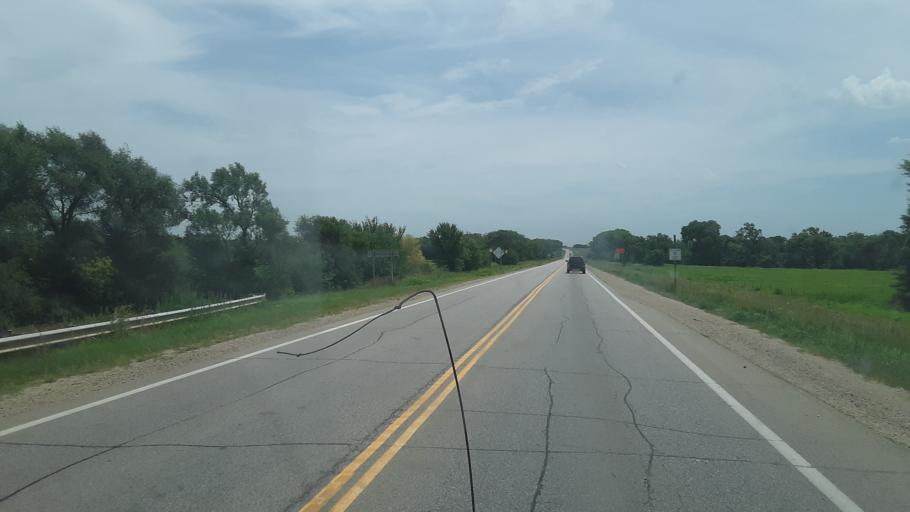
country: US
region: Kansas
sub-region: Butler County
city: El Dorado
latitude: 37.8144
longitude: -96.8290
